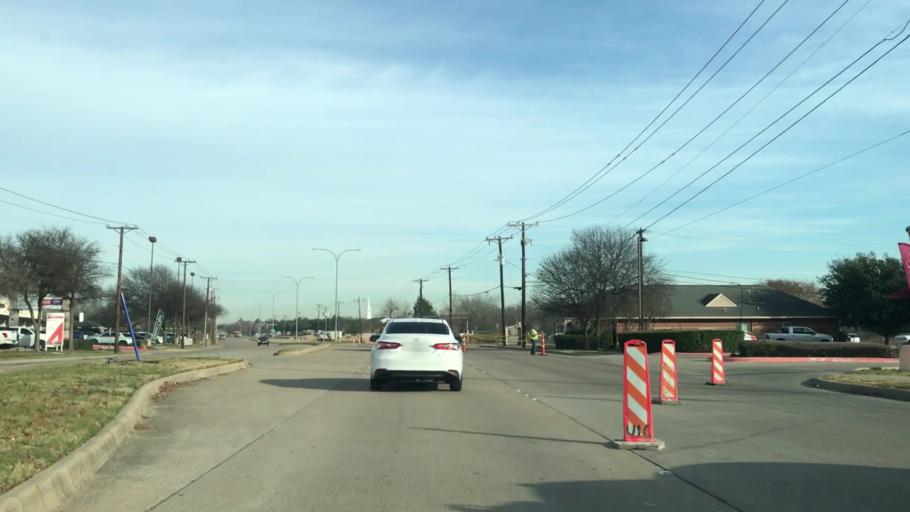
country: US
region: Texas
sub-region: Tarrant County
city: Watauga
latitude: 32.8735
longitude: -97.2899
